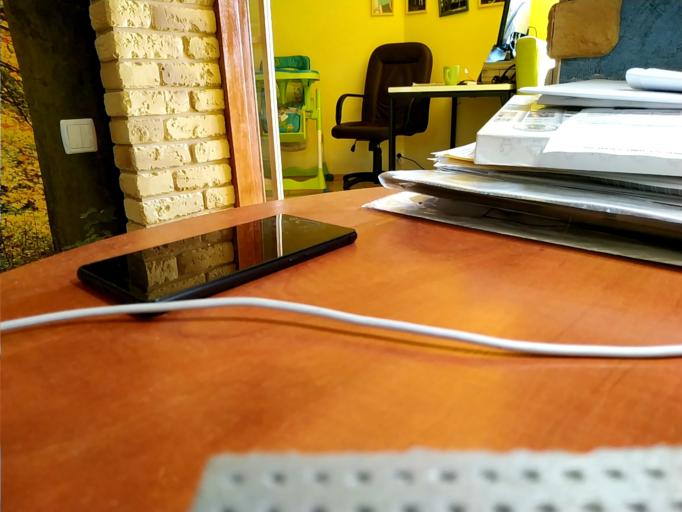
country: RU
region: Tverskaya
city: Kalashnikovo
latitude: 57.3793
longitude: 35.3603
